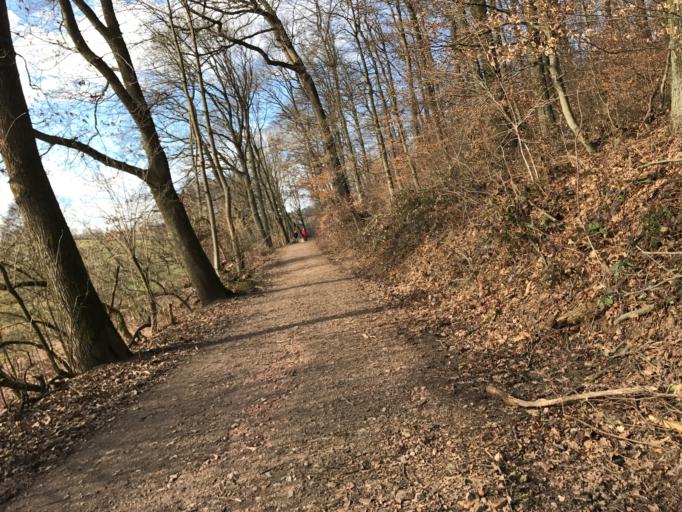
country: DE
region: Hesse
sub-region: Regierungsbezirk Darmstadt
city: Niedernhausen
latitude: 50.0982
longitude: 8.3280
